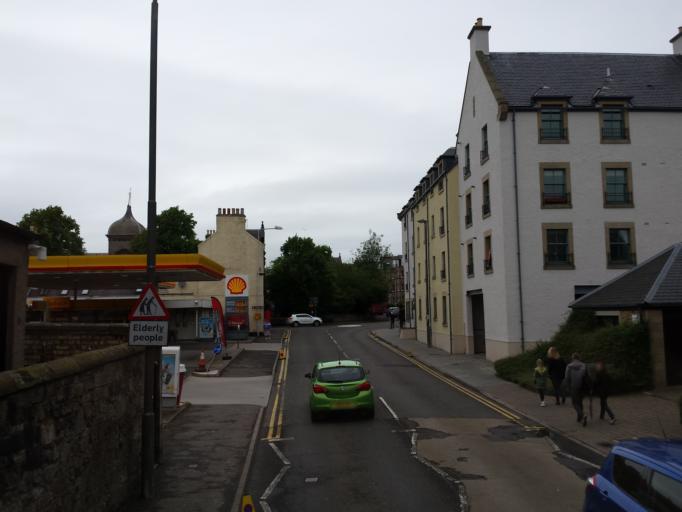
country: GB
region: Scotland
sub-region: Fife
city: Saint Andrews
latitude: 56.3380
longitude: -2.8010
